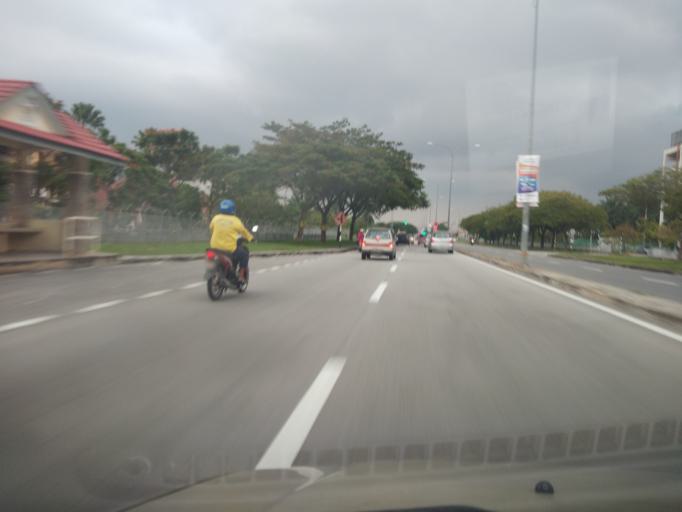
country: MY
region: Penang
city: Kepala Batas
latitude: 5.5192
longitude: 100.4685
